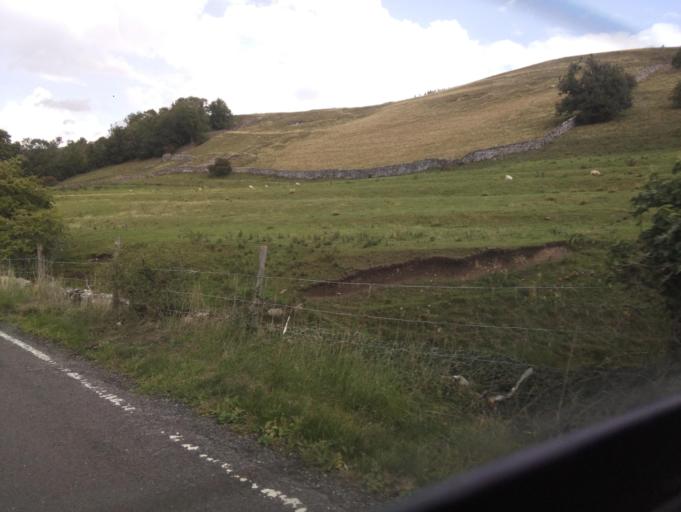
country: GB
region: England
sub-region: North Yorkshire
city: Leyburn
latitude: 54.3798
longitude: -1.8303
